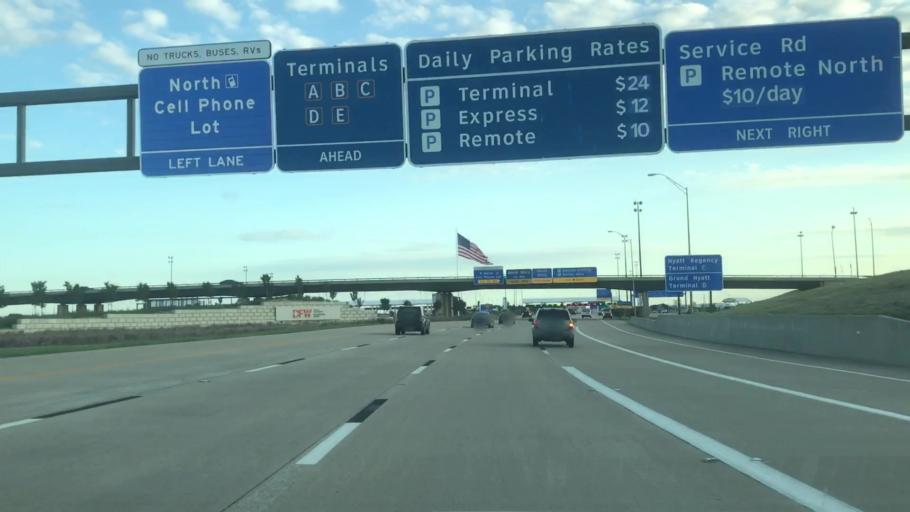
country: US
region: Texas
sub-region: Dallas County
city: Coppell
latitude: 32.9278
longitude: -97.0410
